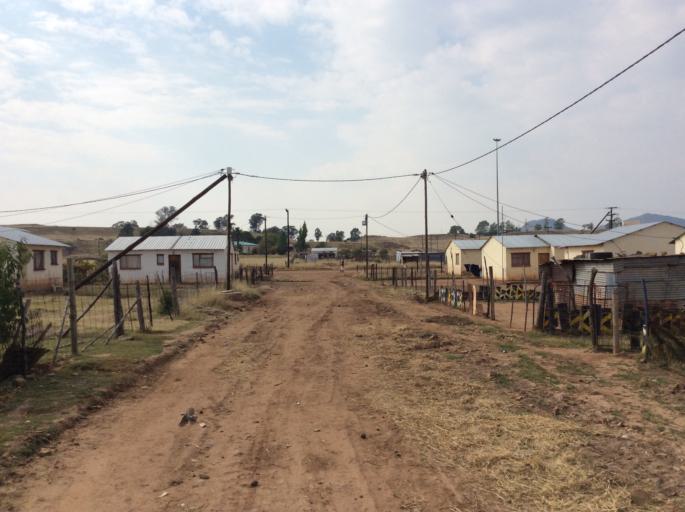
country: LS
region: Mafeteng
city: Mafeteng
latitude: -29.9895
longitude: 27.0013
